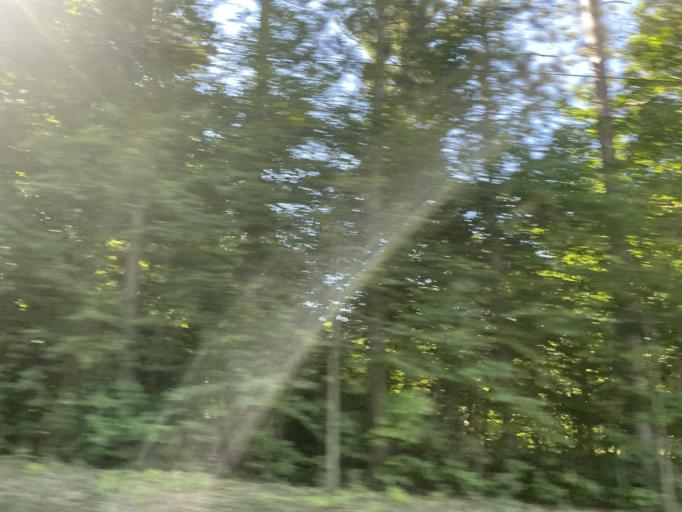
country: US
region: Michigan
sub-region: Benzie County
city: Beulah
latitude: 44.6172
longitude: -86.0494
